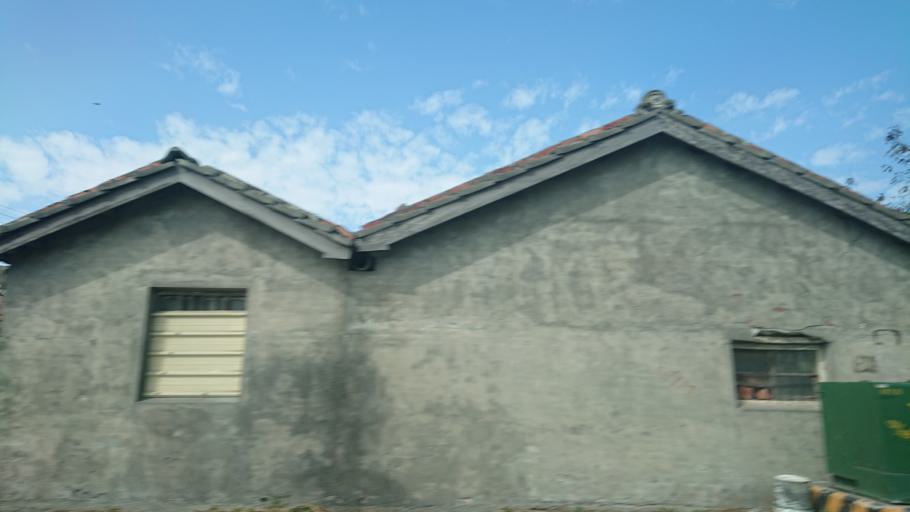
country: TW
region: Taiwan
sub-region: Changhua
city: Chang-hua
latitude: 23.9049
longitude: 120.3079
